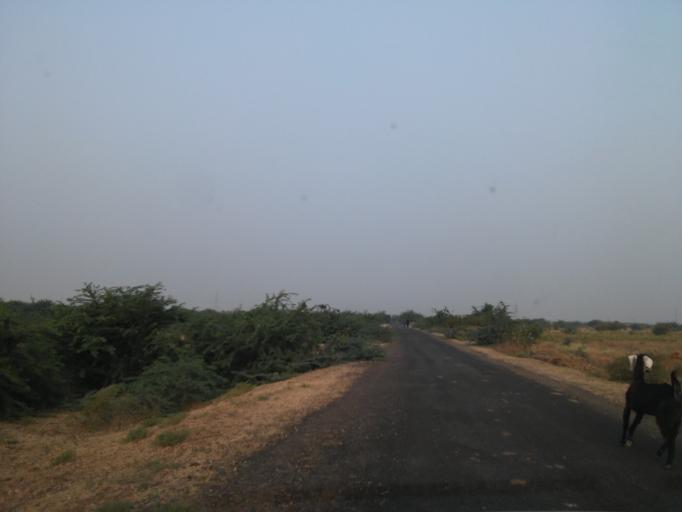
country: PK
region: Sindh
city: Diplo
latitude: 23.9339
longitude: 69.7288
